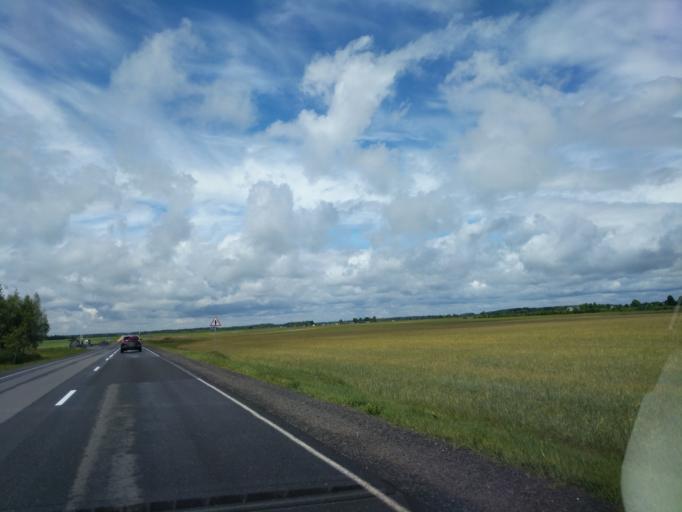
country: BY
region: Minsk
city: Il'ya
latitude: 54.3872
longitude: 27.3575
